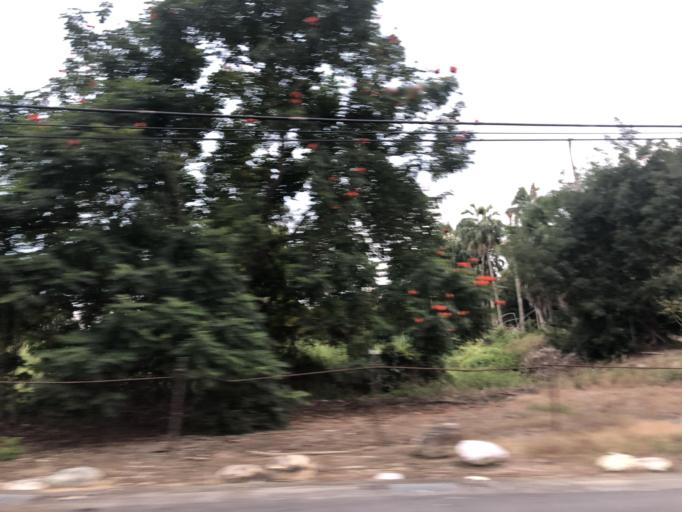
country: TW
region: Taiwan
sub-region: Tainan
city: Tainan
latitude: 23.0254
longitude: 120.3381
